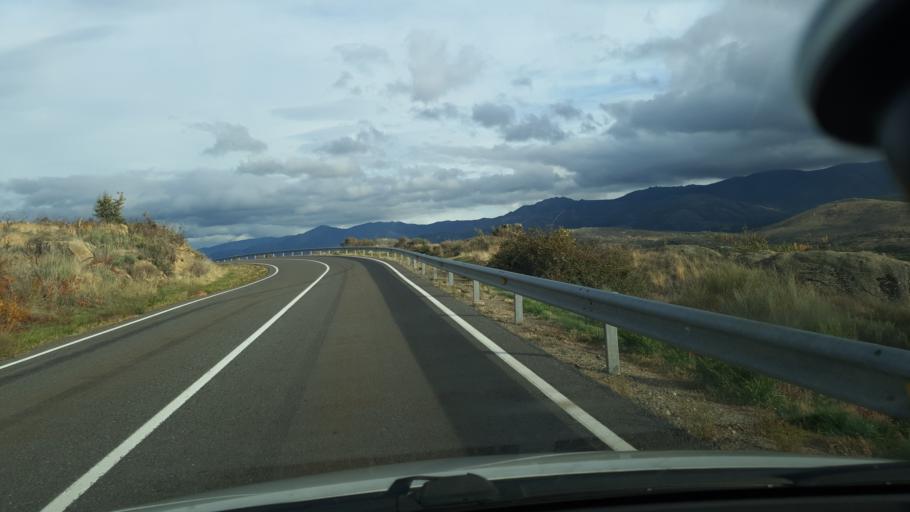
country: ES
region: Castille and Leon
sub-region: Provincia de Avila
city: Hoyocasero
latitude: 40.3917
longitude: -4.9562
